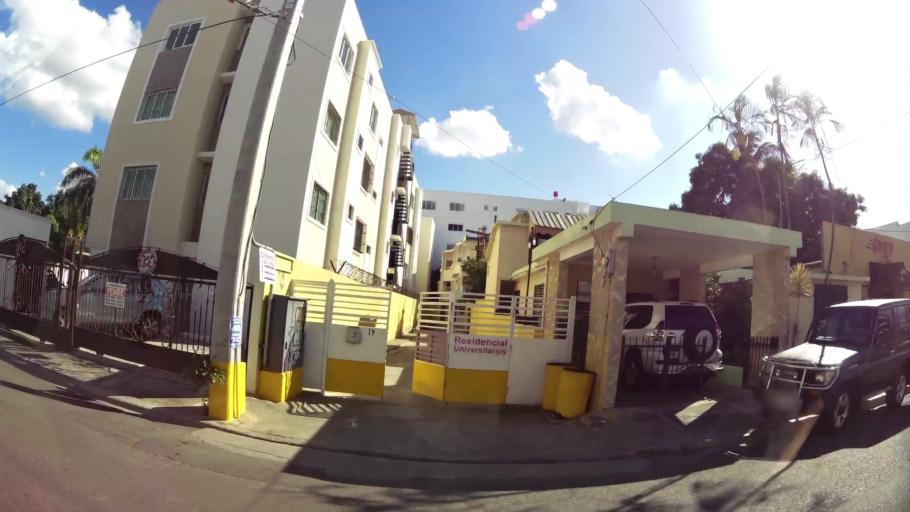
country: DO
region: Santiago
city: Santiago de los Caballeros
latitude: 19.4508
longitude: -70.6769
